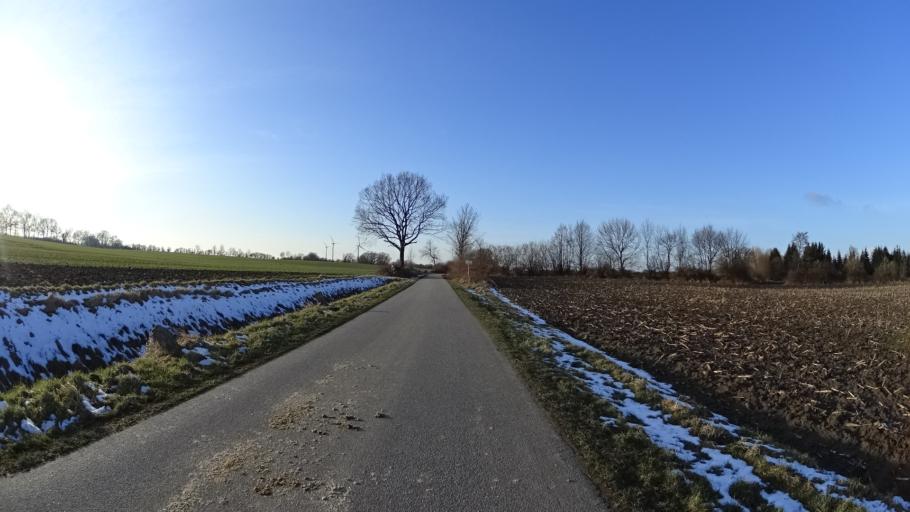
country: DE
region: Schleswig-Holstein
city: Fargau-Pratjau
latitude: 54.3474
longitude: 10.4161
